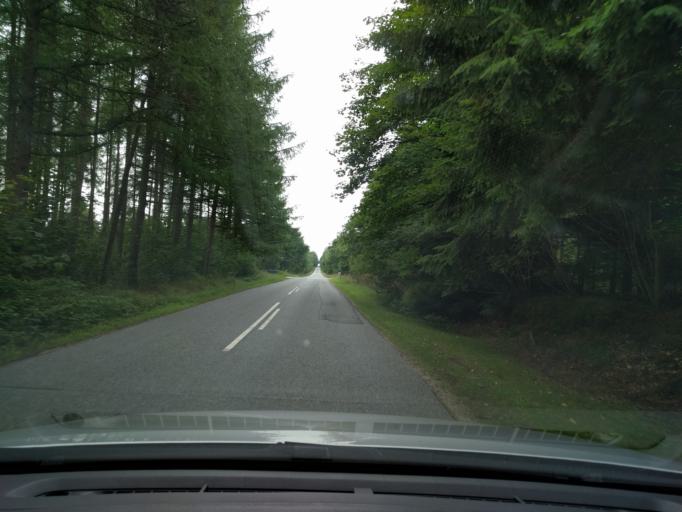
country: DK
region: Central Jutland
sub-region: Herning Kommune
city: Lind
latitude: 56.0375
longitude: 8.9385
